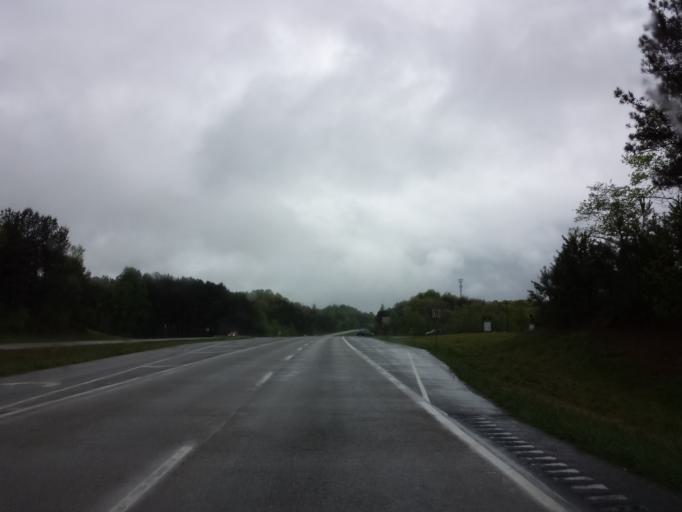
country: US
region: Georgia
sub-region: Pickens County
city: Jasper
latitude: 34.4392
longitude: -84.4387
